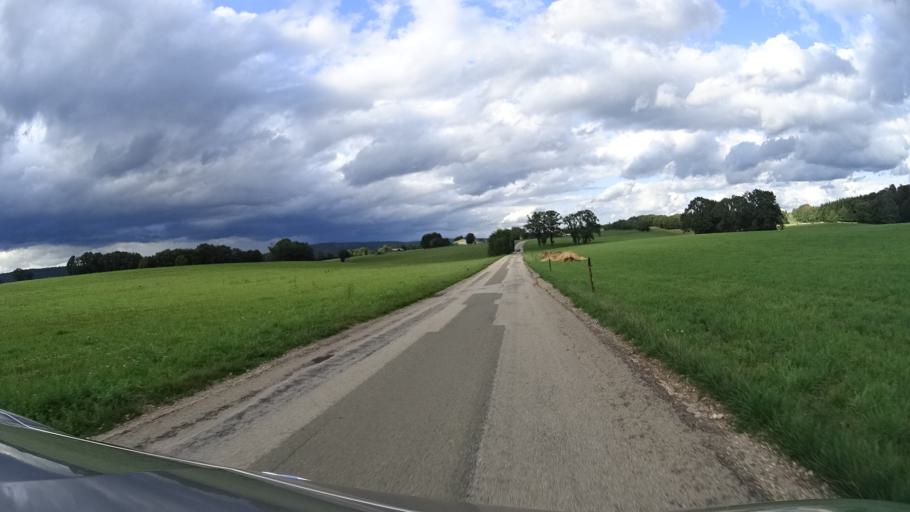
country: FR
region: Franche-Comte
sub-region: Departement du Doubs
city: Nancray
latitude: 47.2348
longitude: 6.1672
